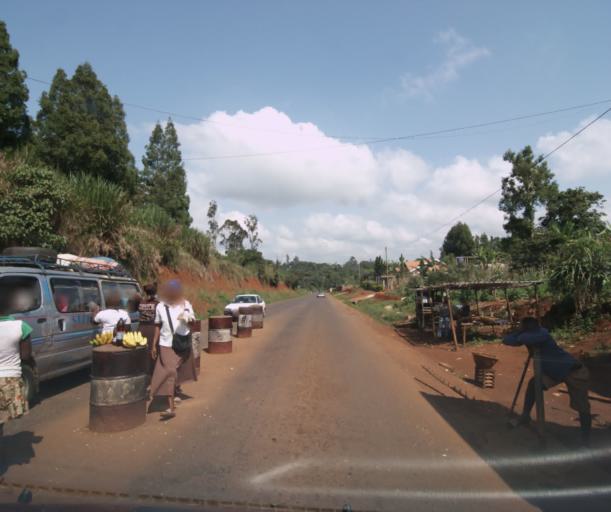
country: CM
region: West
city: Bansoa
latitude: 5.4907
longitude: 10.1900
